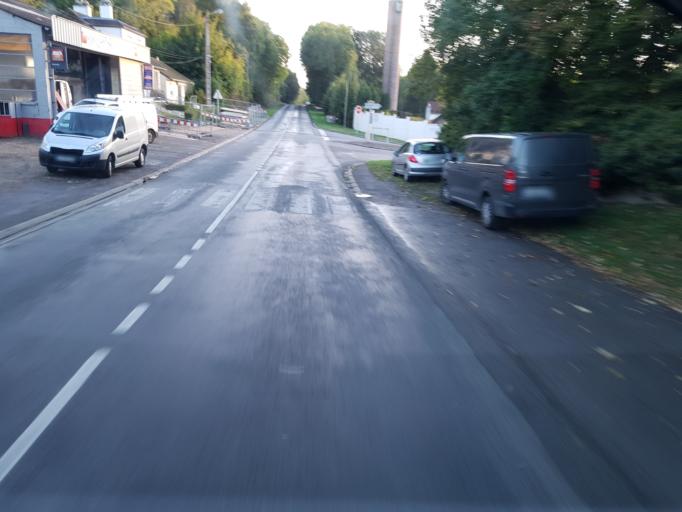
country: FR
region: Picardie
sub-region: Departement de la Somme
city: Saleux
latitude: 49.8291
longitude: 2.2285
